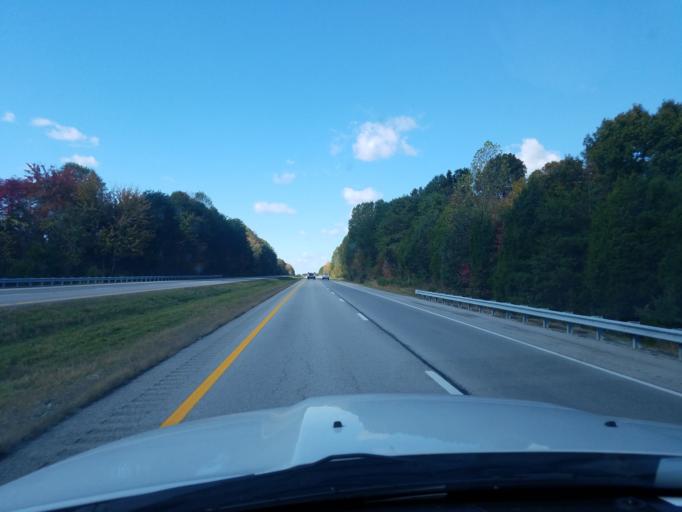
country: US
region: Kentucky
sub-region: Barren County
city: Glasgow
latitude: 36.9973
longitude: -85.8036
